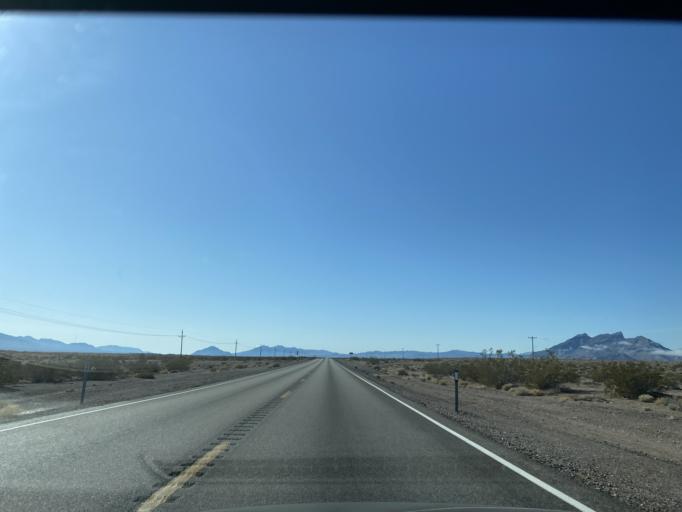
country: US
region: Nevada
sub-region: Nye County
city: Pahrump
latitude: 36.4682
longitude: -116.4216
